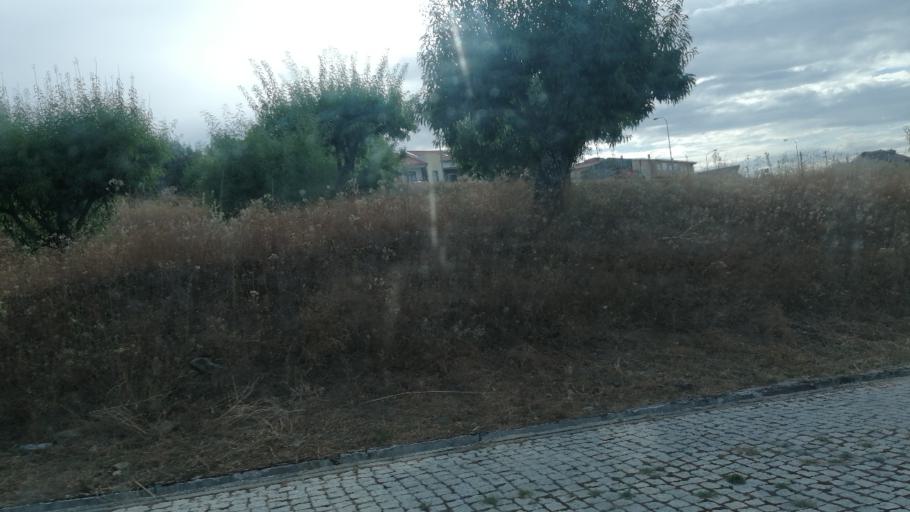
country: PT
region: Viseu
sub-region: Sao Joao da Pesqueira
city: Sao Joao da Pesqueira
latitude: 41.1437
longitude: -7.4024
